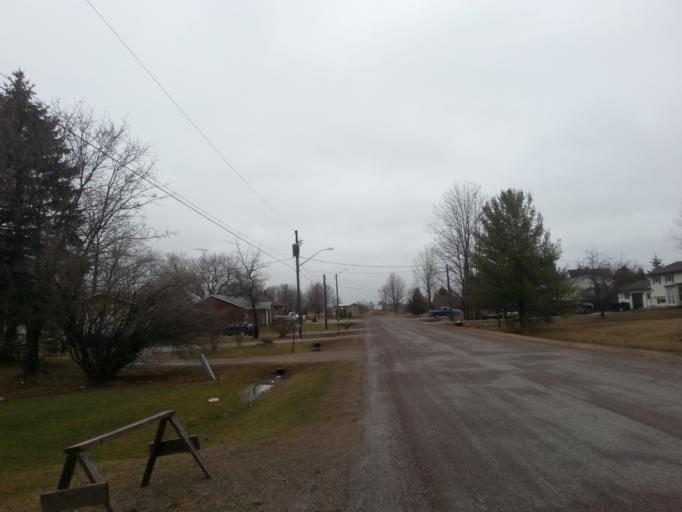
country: CA
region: Ontario
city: Orillia
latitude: 44.5505
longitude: -79.1765
